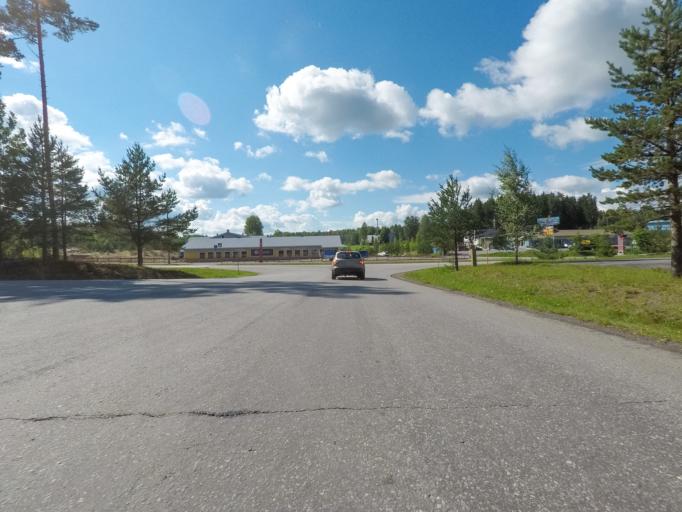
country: FI
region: Southern Savonia
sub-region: Mikkeli
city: Pertunmaa
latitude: 61.4224
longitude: 26.4351
